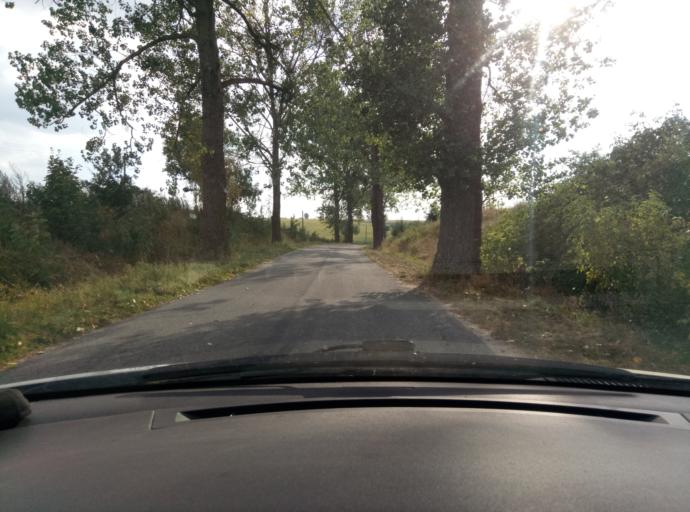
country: PL
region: Kujawsko-Pomorskie
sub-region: Powiat brodnicki
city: Jablonowo Pomorskie
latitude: 53.3876
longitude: 19.2212
